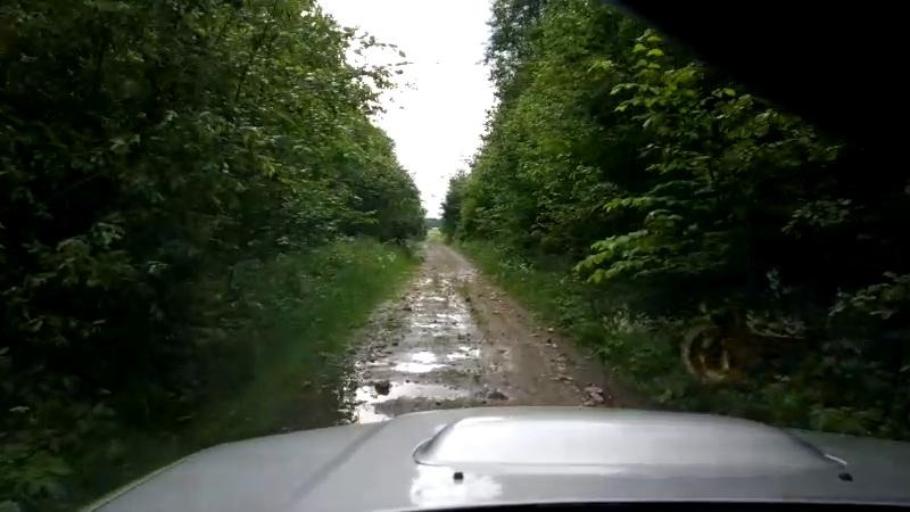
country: EE
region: Paernumaa
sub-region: Halinga vald
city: Parnu-Jaagupi
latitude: 58.5655
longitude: 24.5618
